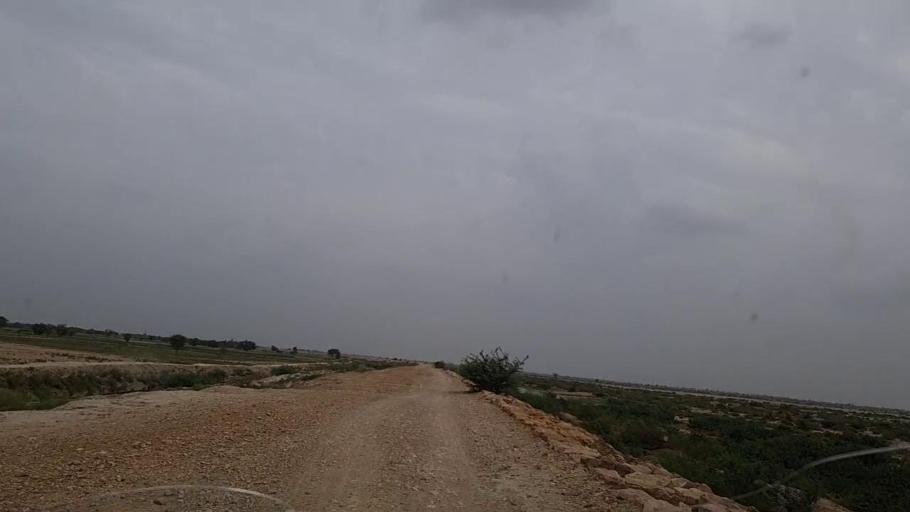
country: PK
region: Sindh
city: Johi
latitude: 26.7136
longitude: 67.5835
